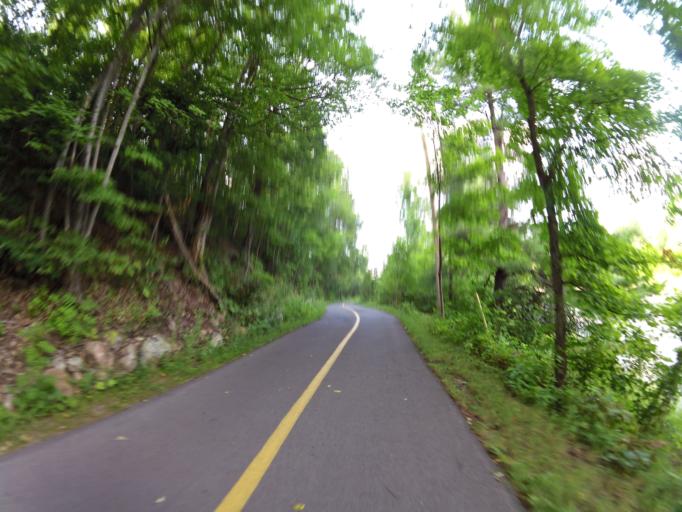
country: CA
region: Quebec
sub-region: Outaouais
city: Gatineau
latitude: 45.4763
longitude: -75.7929
